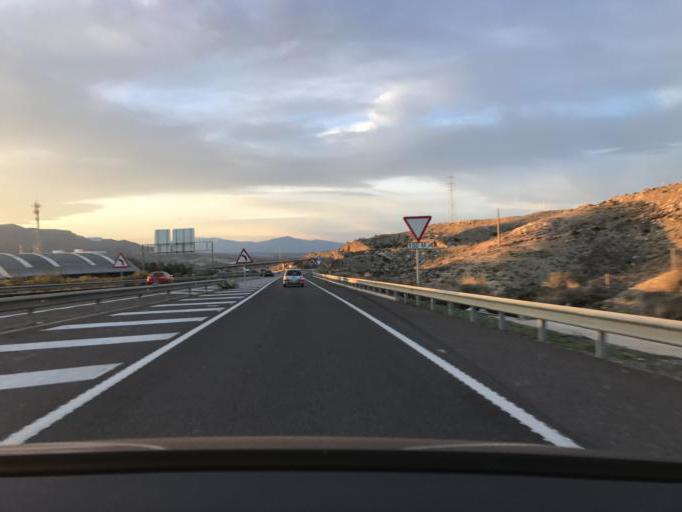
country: ES
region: Andalusia
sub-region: Provincia de Almeria
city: Viator
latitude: 36.8905
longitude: -2.4192
